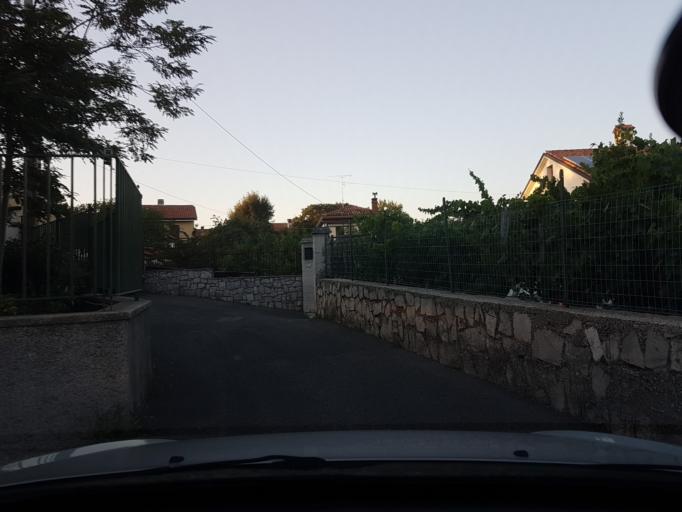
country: IT
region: Friuli Venezia Giulia
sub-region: Provincia di Trieste
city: Santa Croce
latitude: 45.7310
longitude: 13.6947
